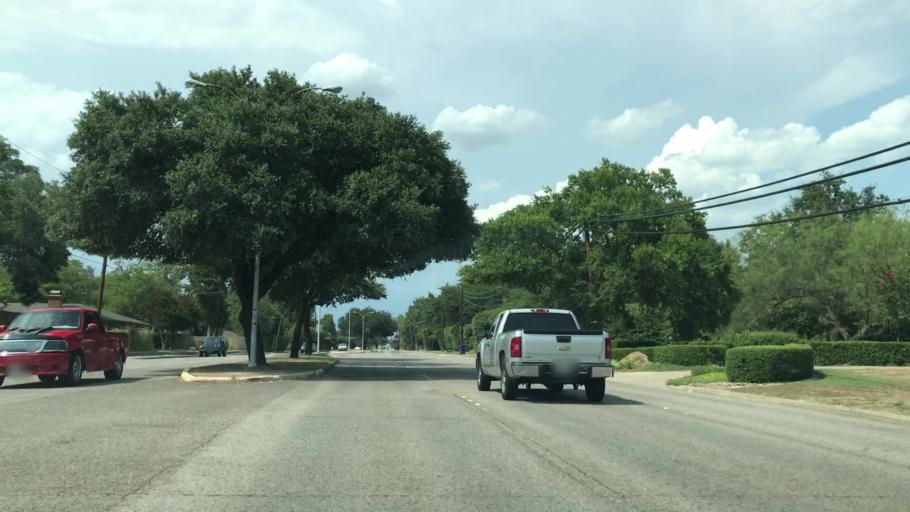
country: US
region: Texas
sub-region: Dallas County
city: Farmers Branch
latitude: 32.9201
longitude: -96.8732
